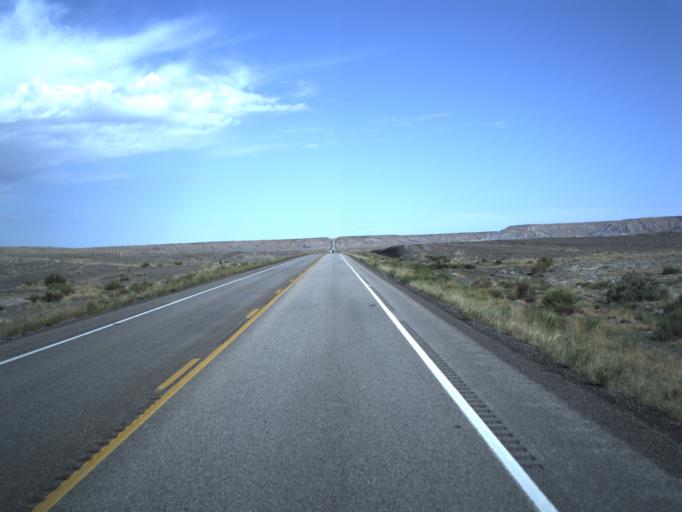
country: US
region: Utah
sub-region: Carbon County
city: East Carbon City
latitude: 39.3553
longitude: -110.3840
